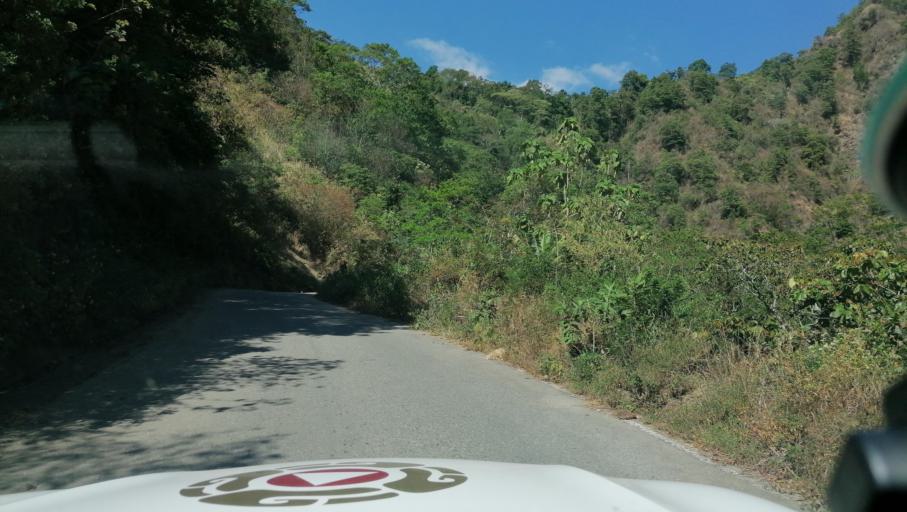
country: MX
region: Chiapas
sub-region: Cacahoatan
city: Benito Juarez
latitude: 15.1818
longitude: -92.1893
